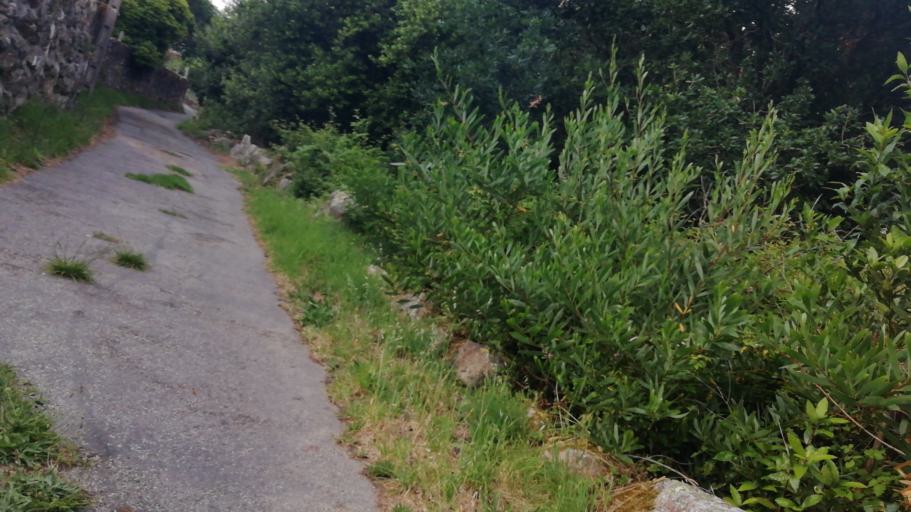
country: ES
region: Galicia
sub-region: Provincia de Pontevedra
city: A Guarda
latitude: 41.8843
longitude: -8.8606
